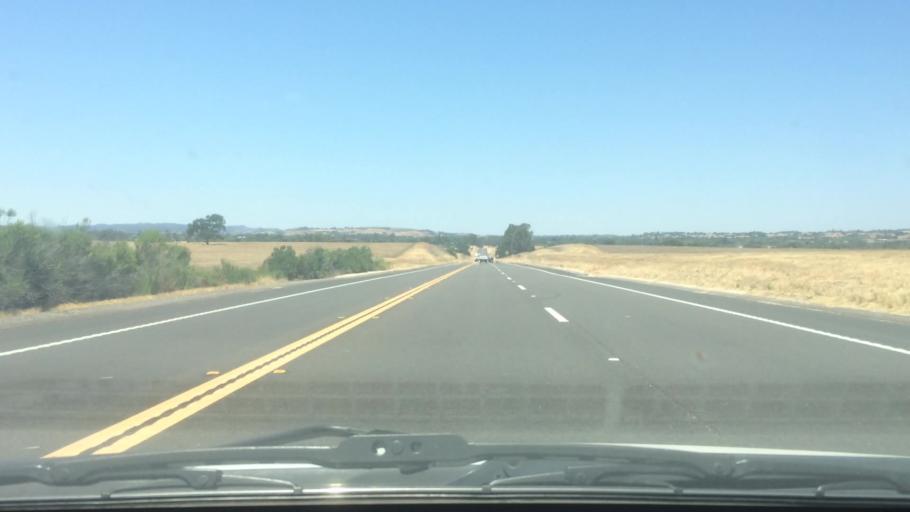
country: US
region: California
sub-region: Santa Barbara County
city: Santa Ynez
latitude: 34.6167
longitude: -120.0632
